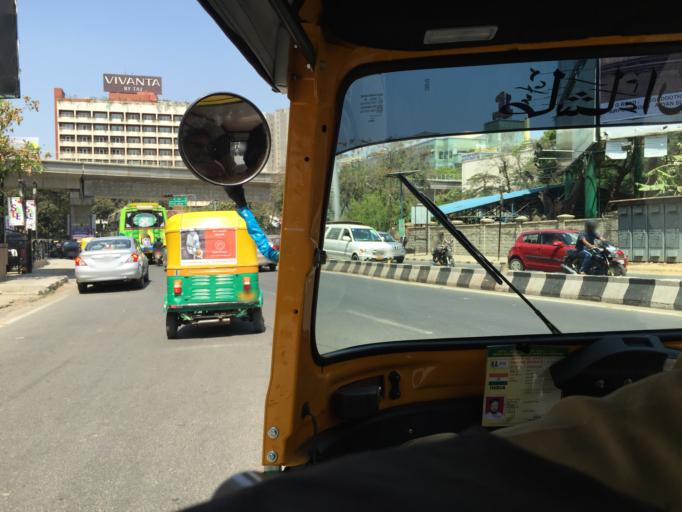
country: IN
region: Karnataka
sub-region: Bangalore Urban
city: Bangalore
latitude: 12.9718
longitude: 77.6195
